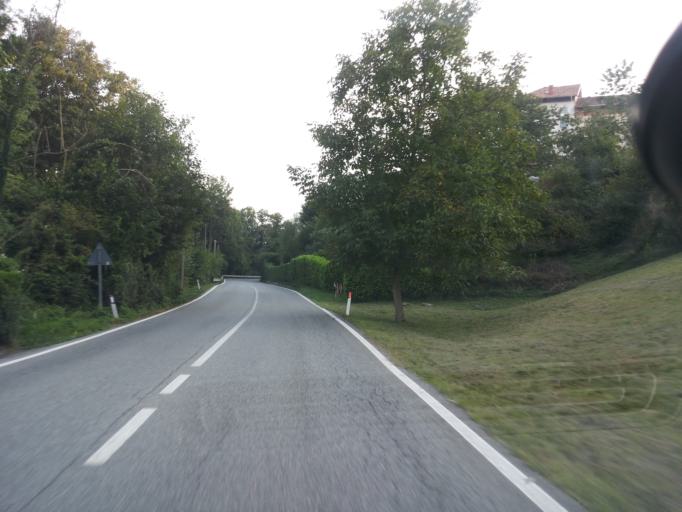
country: IT
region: Piedmont
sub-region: Provincia di Biella
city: Mosso
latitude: 45.6539
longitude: 8.1543
